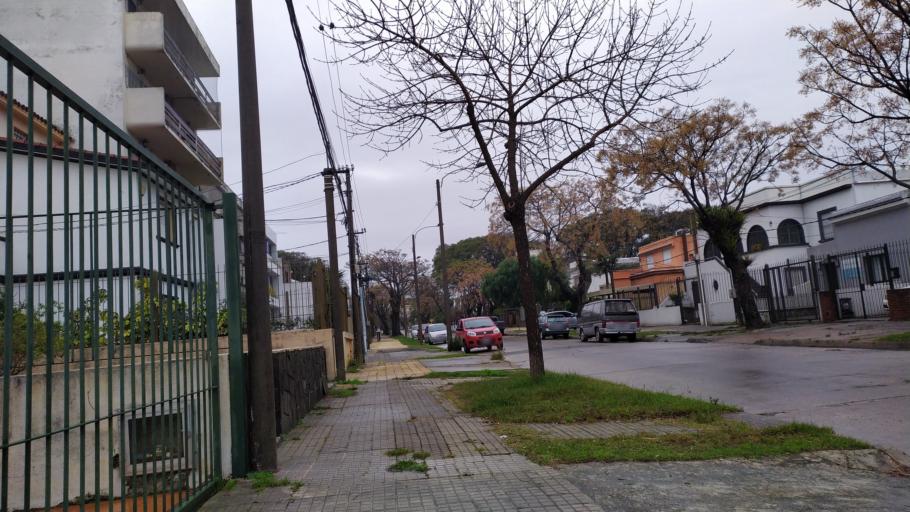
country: UY
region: Canelones
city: Paso de Carrasco
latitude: -34.8939
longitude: -56.1010
